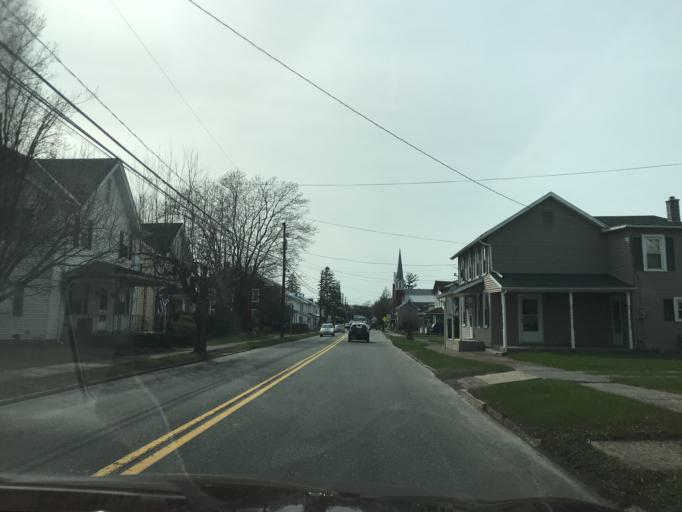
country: US
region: Pennsylvania
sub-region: Union County
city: Lewisburg
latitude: 40.9657
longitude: -76.8531
